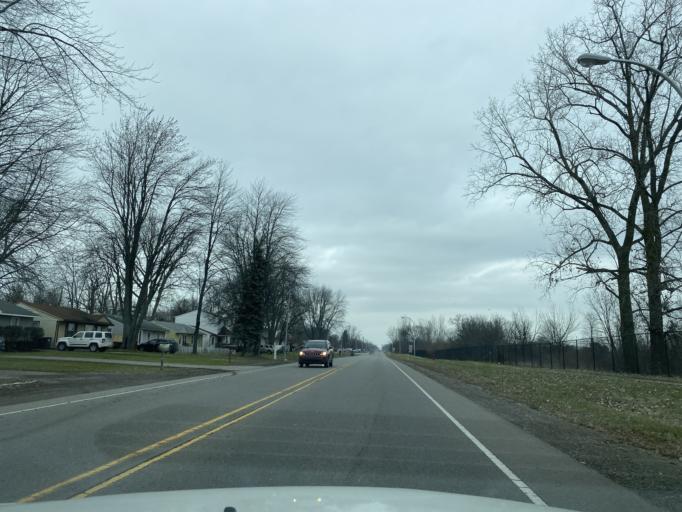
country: US
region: Michigan
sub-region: Wayne County
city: Taylor
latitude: 42.2023
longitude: -83.2873
